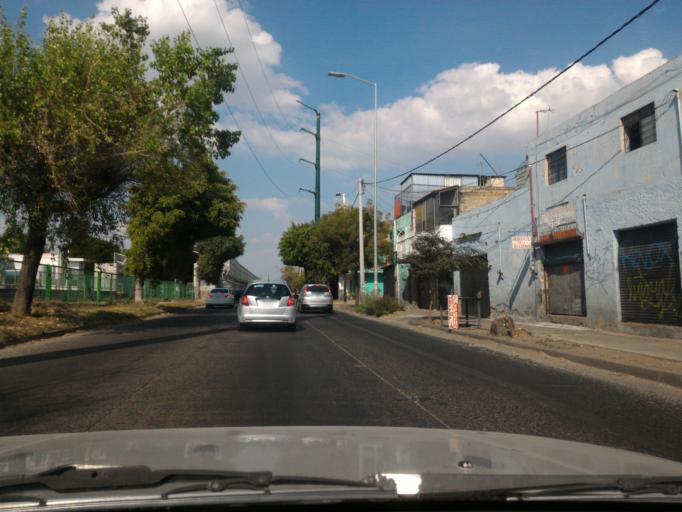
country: MX
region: Jalisco
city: Guadalajara
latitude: 20.6369
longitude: -103.3776
